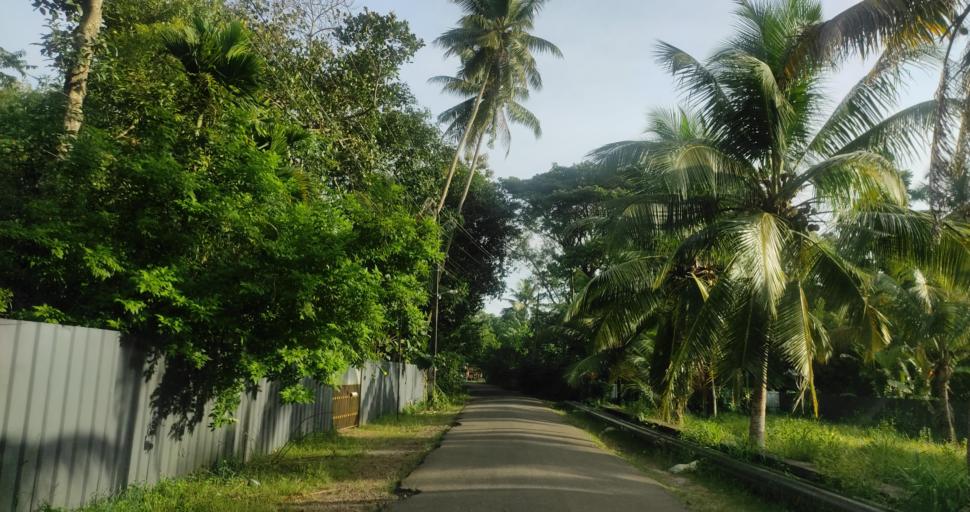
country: IN
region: Kerala
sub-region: Alappuzha
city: Shertallai
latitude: 9.6344
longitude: 76.3430
